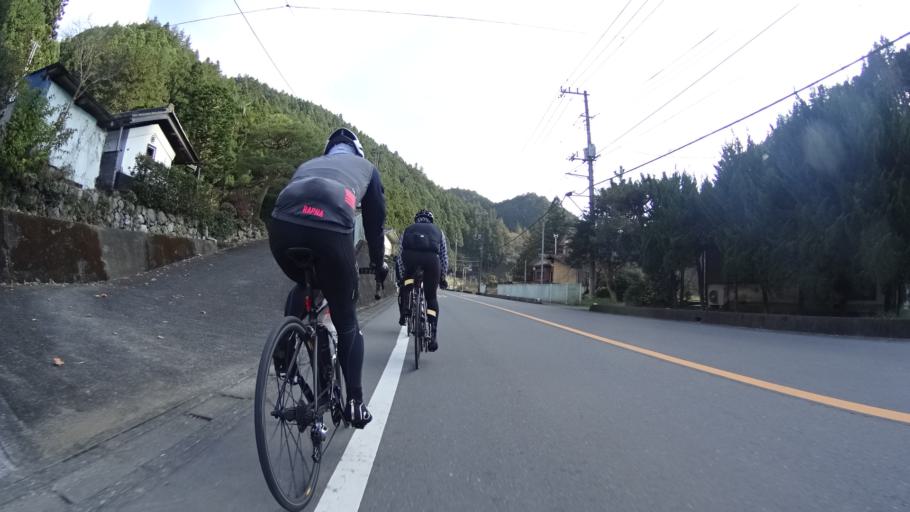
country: JP
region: Tokyo
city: Ome
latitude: 35.8751
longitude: 139.1866
